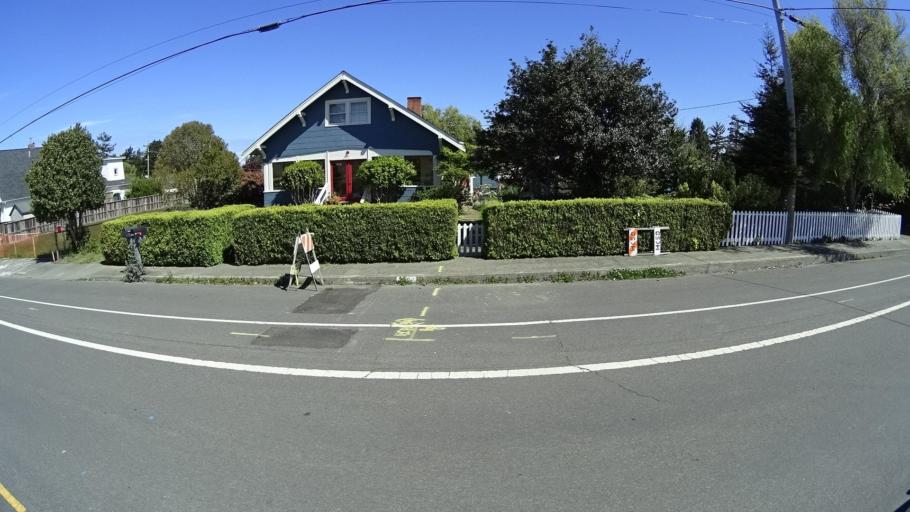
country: US
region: California
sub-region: Humboldt County
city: Myrtletown
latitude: 40.7951
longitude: -124.1295
